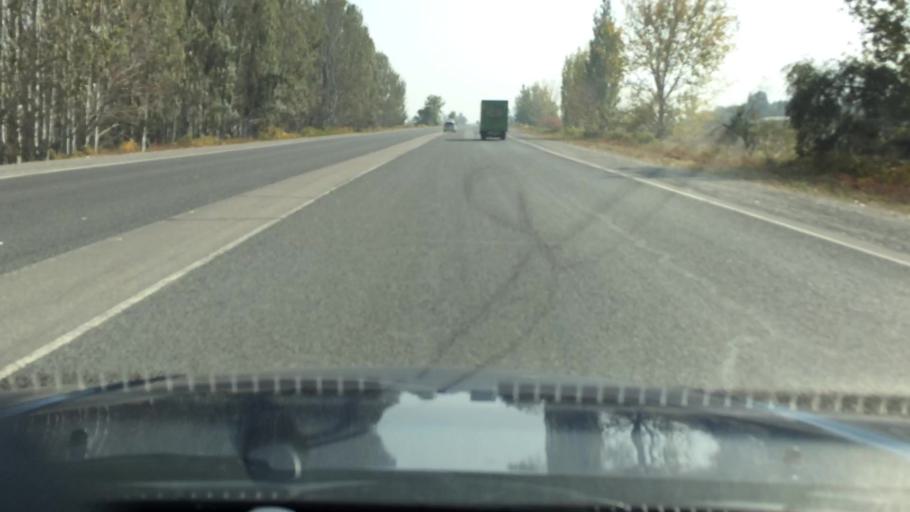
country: KG
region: Chuy
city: Ivanovka
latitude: 42.9356
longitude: 74.9919
